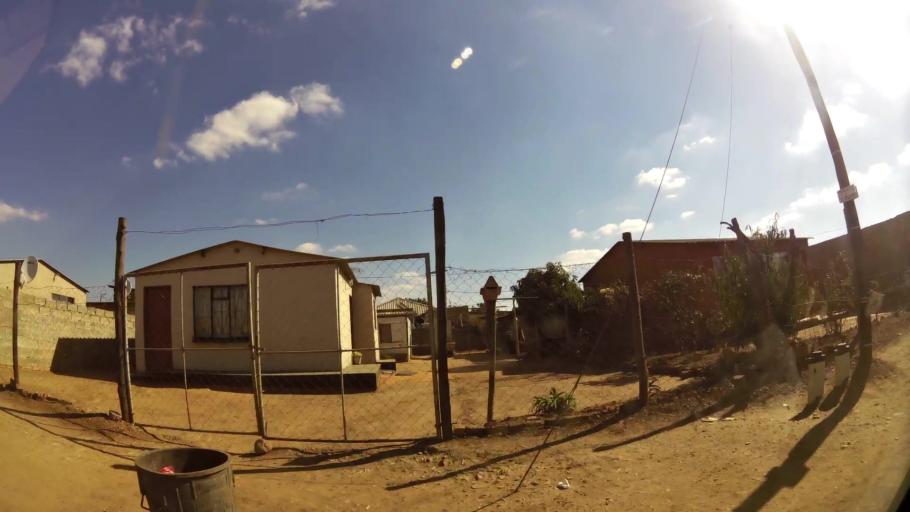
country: ZA
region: Gauteng
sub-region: City of Tshwane Metropolitan Municipality
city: Cullinan
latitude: -25.7194
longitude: 28.4098
